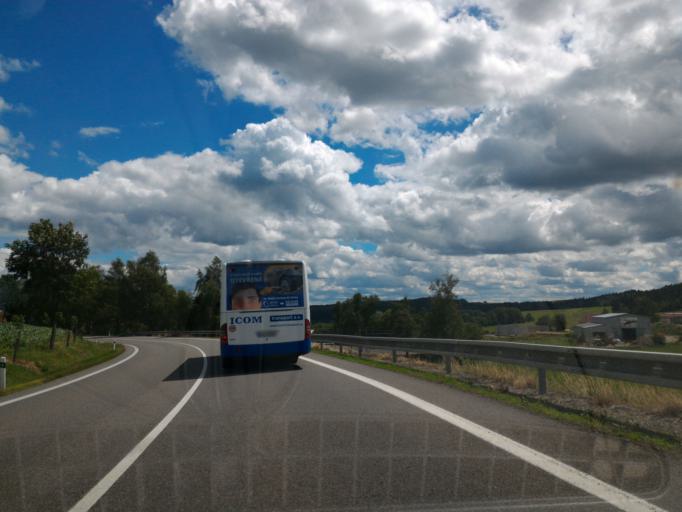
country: CZ
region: Vysocina
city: Bohdalov
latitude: 49.4770
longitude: 15.8267
